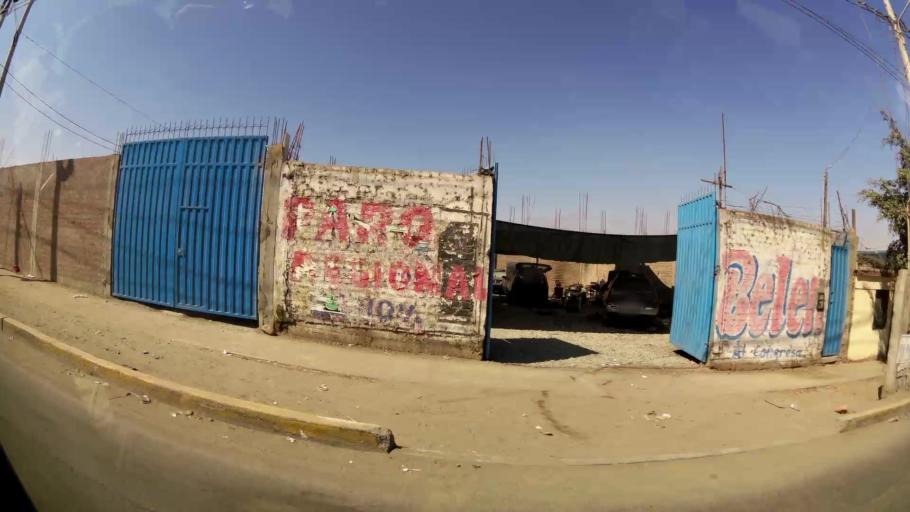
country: PE
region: Ica
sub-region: Provincia de Ica
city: Ica
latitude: -14.0600
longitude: -75.7167
